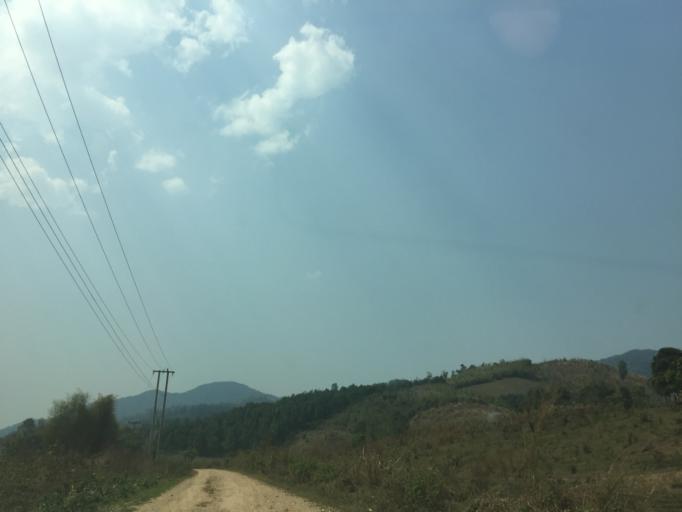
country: TH
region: Nan
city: Song Khwae
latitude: 19.7346
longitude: 100.7251
